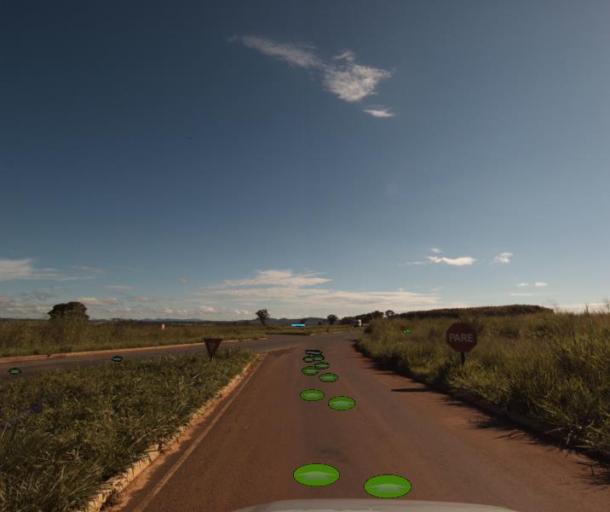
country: BR
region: Goias
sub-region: Uruacu
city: Uruacu
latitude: -14.6349
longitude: -49.1761
